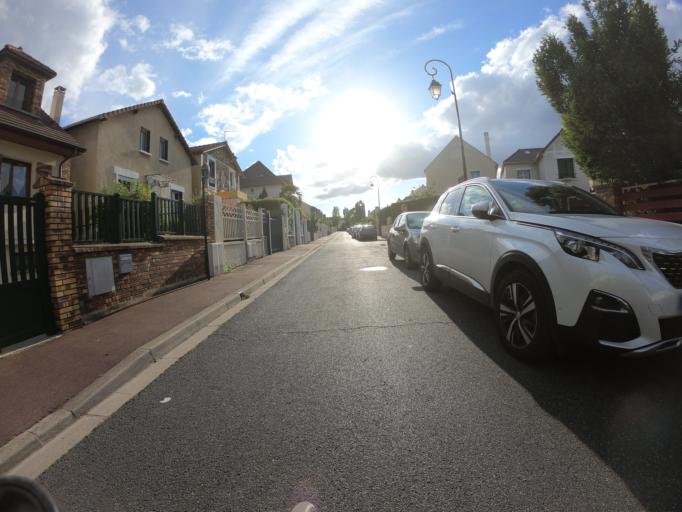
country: FR
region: Ile-de-France
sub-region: Departement des Hauts-de-Seine
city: Antony
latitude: 48.7443
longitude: 2.3070
